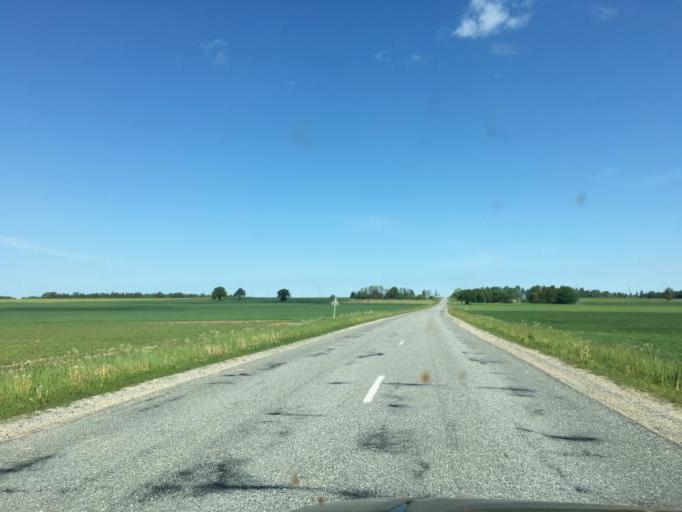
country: LV
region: Talsu Rajons
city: Valdemarpils
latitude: 57.3501
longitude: 22.4977
